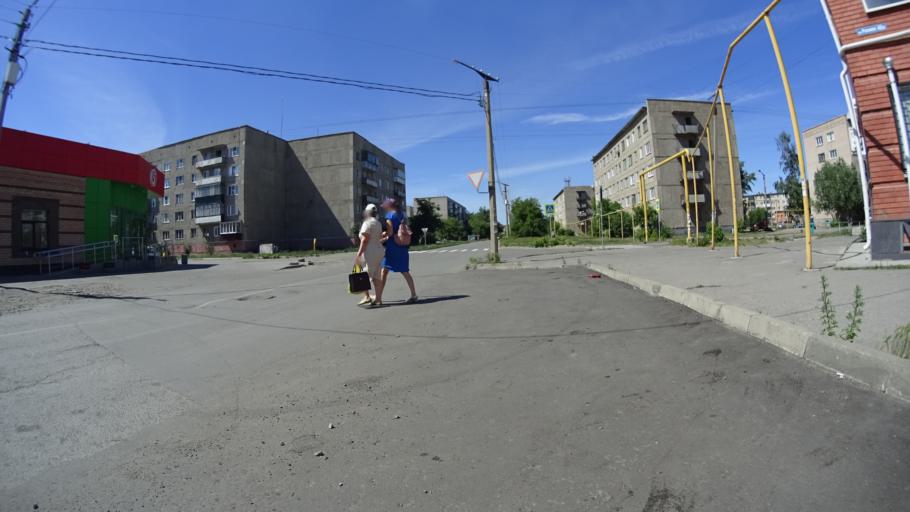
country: RU
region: Chelyabinsk
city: Troitsk
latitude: 54.0910
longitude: 61.5508
